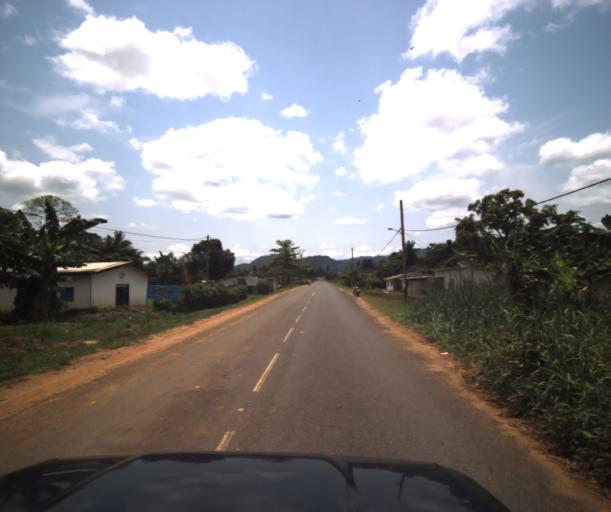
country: CM
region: Centre
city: Eseka
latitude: 3.6502
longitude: 10.7864
